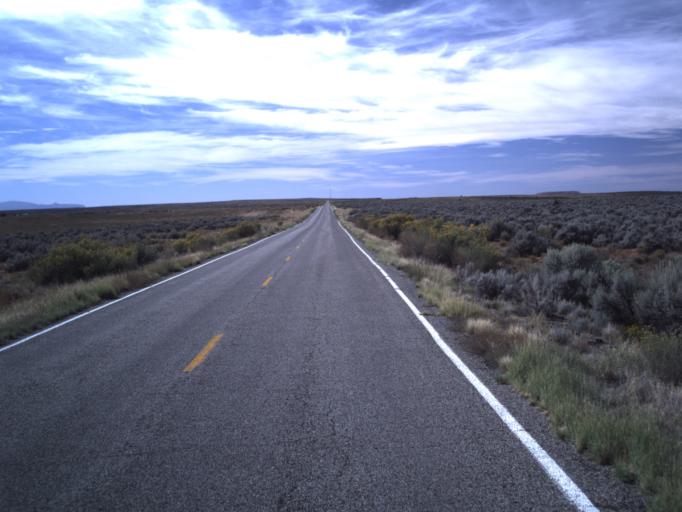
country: US
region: Utah
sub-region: San Juan County
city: Blanding
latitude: 37.3796
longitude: -109.3416
